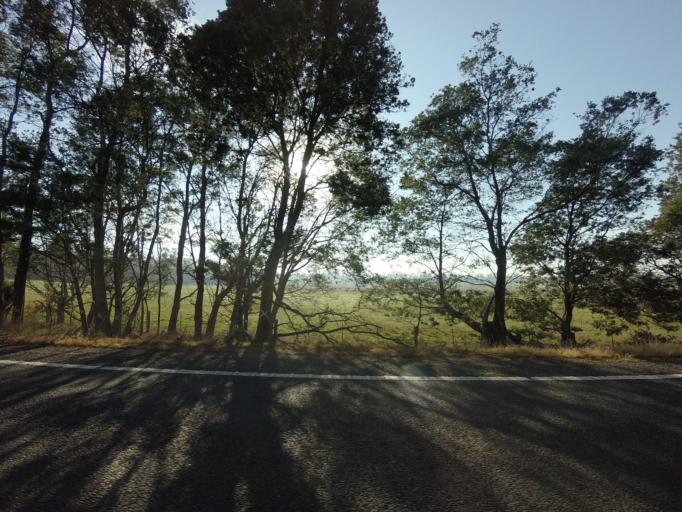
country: AU
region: Tasmania
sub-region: Northern Midlands
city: Longford
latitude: -41.5397
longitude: 147.0515
